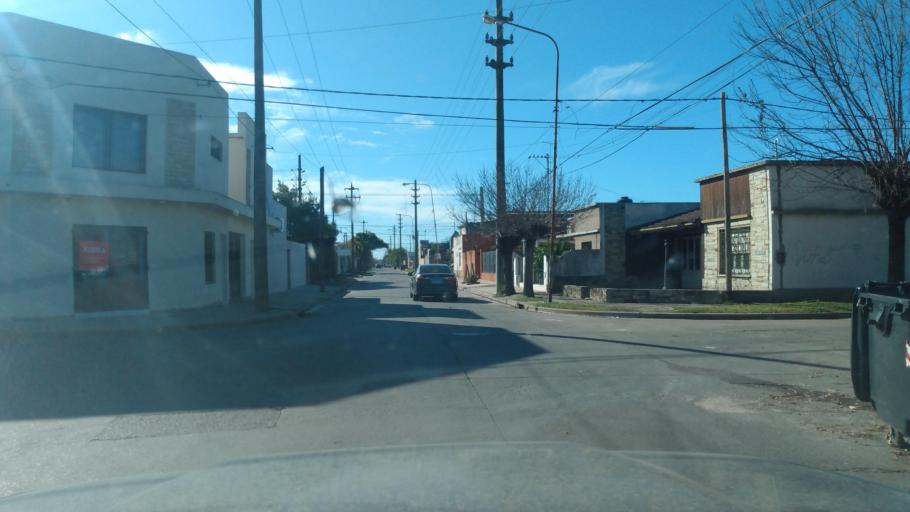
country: AR
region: Buenos Aires
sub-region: Partido de Lujan
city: Lujan
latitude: -34.5665
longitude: -59.0958
